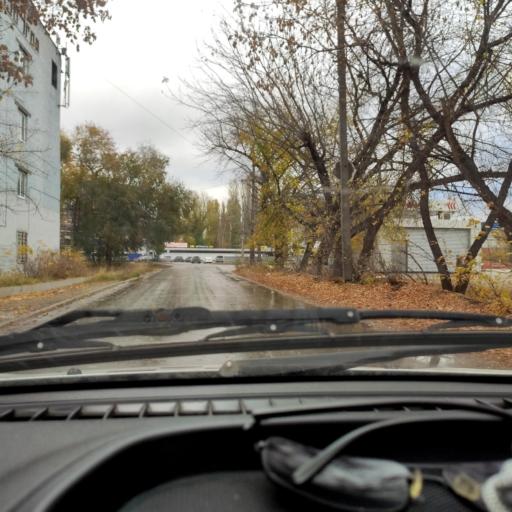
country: RU
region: Samara
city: Tol'yatti
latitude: 53.5169
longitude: 49.4553
